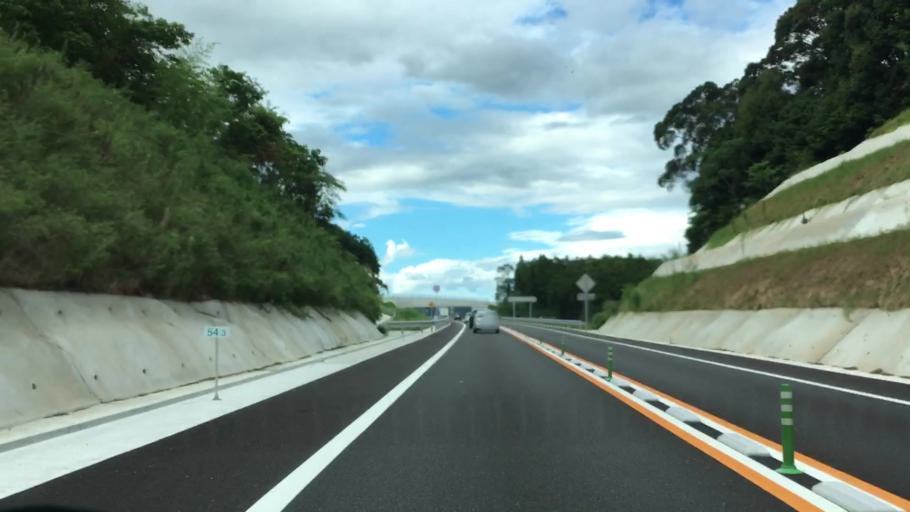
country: JP
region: Saga Prefecture
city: Imaricho-ko
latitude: 33.3287
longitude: 129.9278
